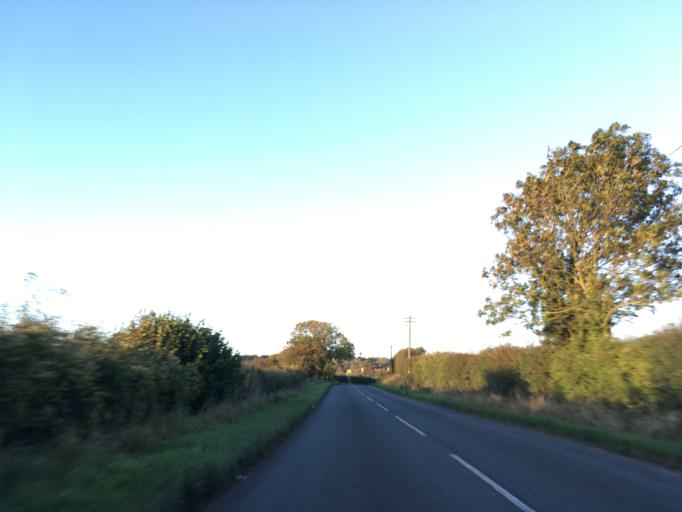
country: GB
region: England
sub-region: South Gloucestershire
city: Almondsbury
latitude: 51.5681
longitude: -2.5697
